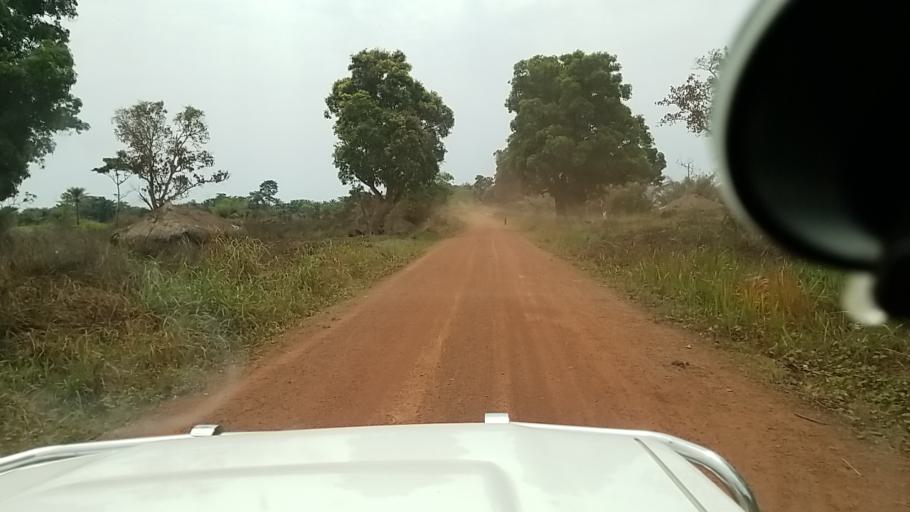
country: CD
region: Equateur
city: Libenge
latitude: 3.7350
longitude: 18.7775
